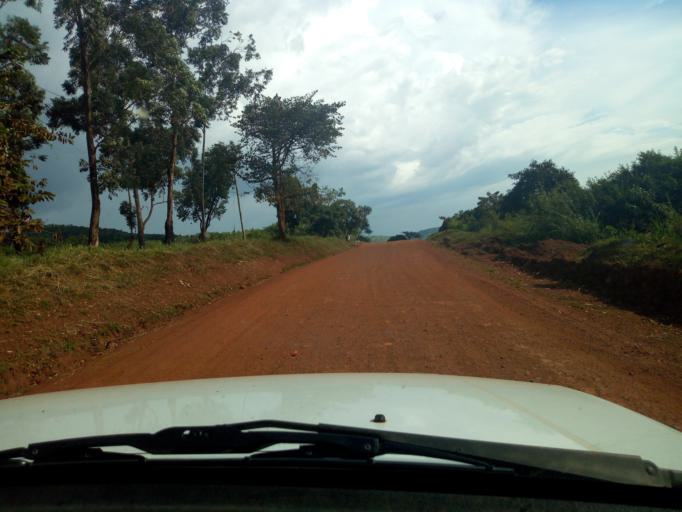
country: UG
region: Western Region
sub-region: Masindi District
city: Masindi
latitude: 1.6564
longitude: 31.7062
